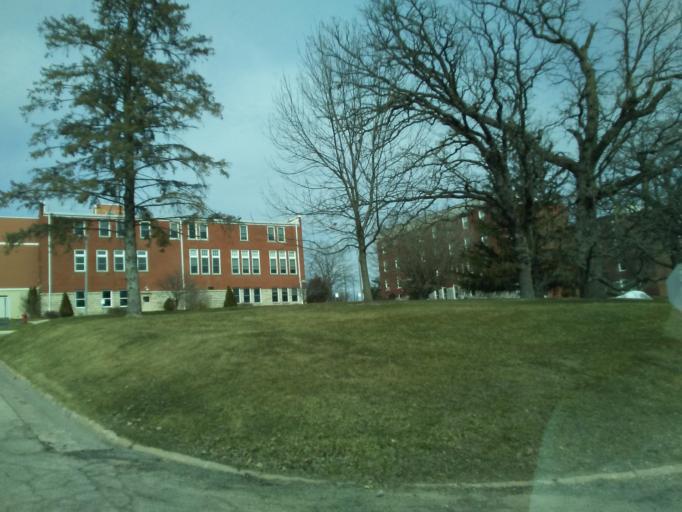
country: US
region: Iowa
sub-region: Winneshiek County
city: Decorah
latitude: 43.3097
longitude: -91.8065
